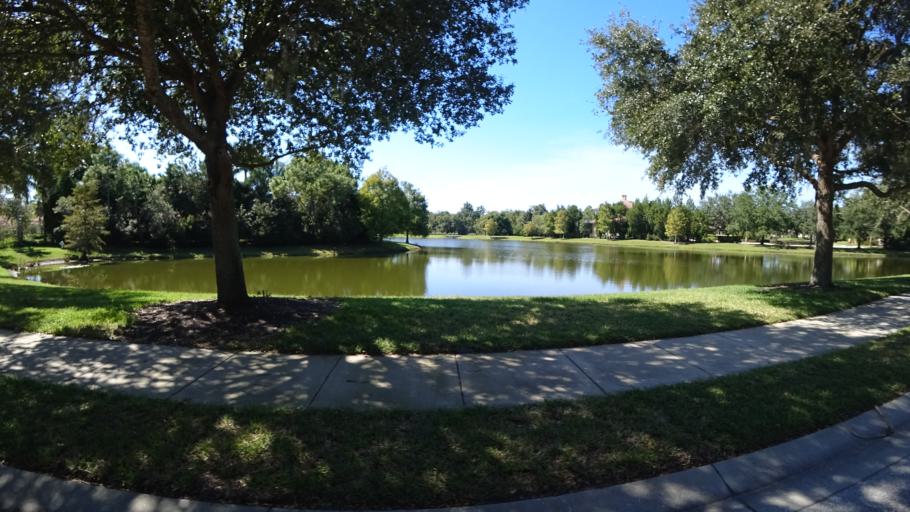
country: US
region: Florida
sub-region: Sarasota County
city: The Meadows
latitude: 27.4121
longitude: -82.4063
